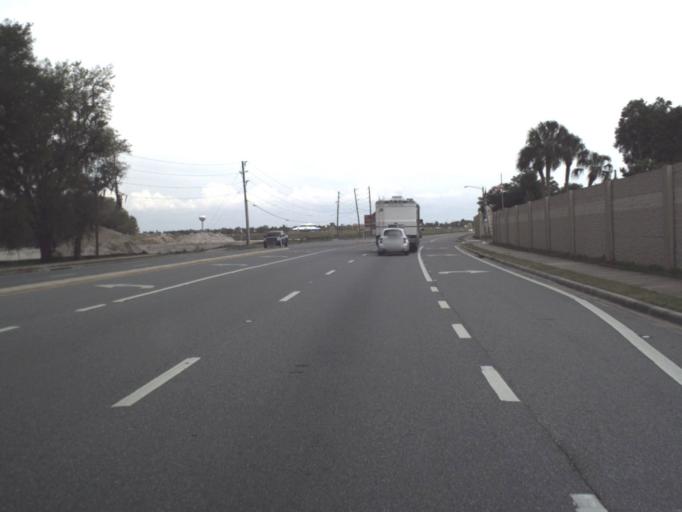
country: US
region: Florida
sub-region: Sumter County
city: Wildwood
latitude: 28.8468
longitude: -82.0399
